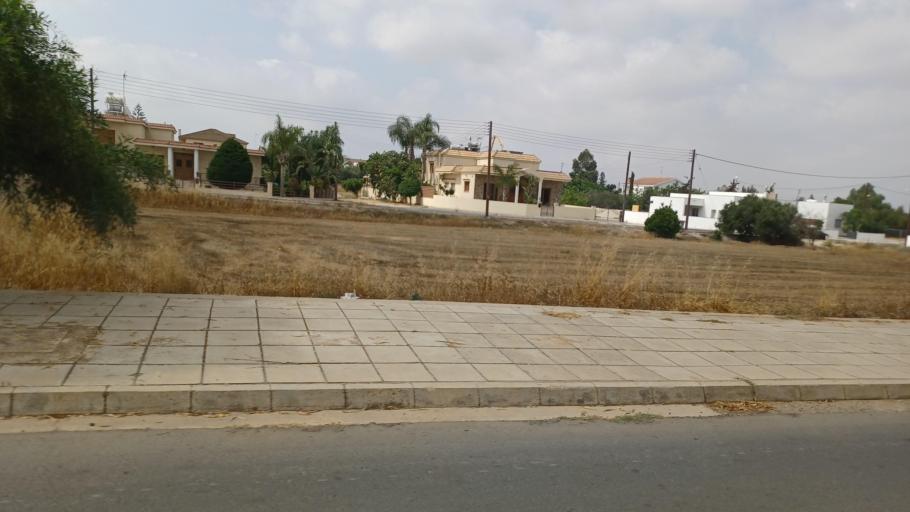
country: CY
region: Ammochostos
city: Deryneia
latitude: 35.0603
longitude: 33.9505
